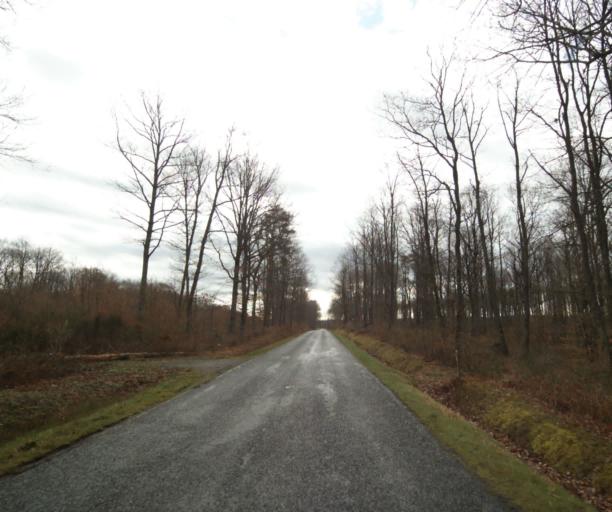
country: FR
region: Auvergne
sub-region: Departement de l'Allier
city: Neuilly-le-Real
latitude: 46.5176
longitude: 3.4371
